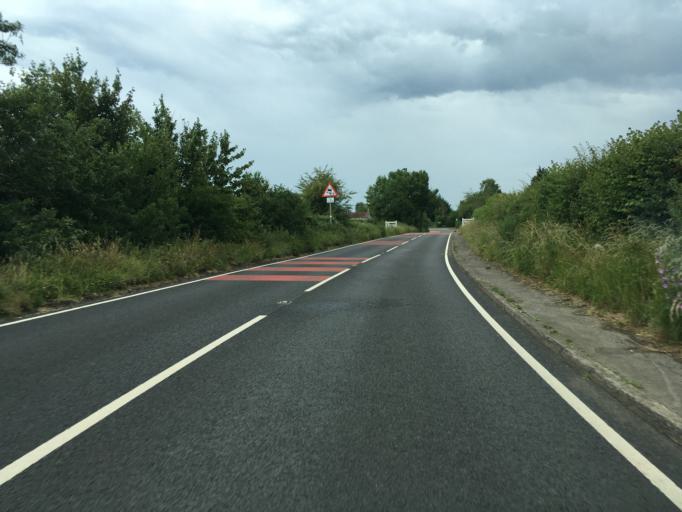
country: GB
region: England
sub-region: Gloucestershire
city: Stonehouse
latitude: 51.7790
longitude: -2.2882
